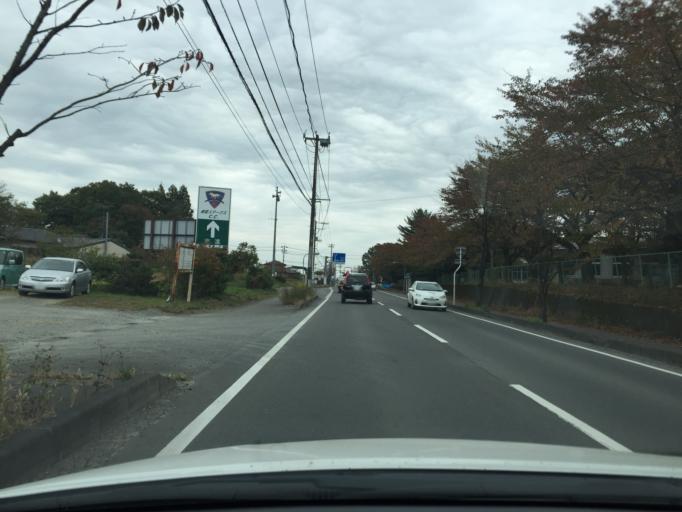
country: JP
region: Tochigi
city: Kuroiso
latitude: 37.1035
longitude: 140.2270
